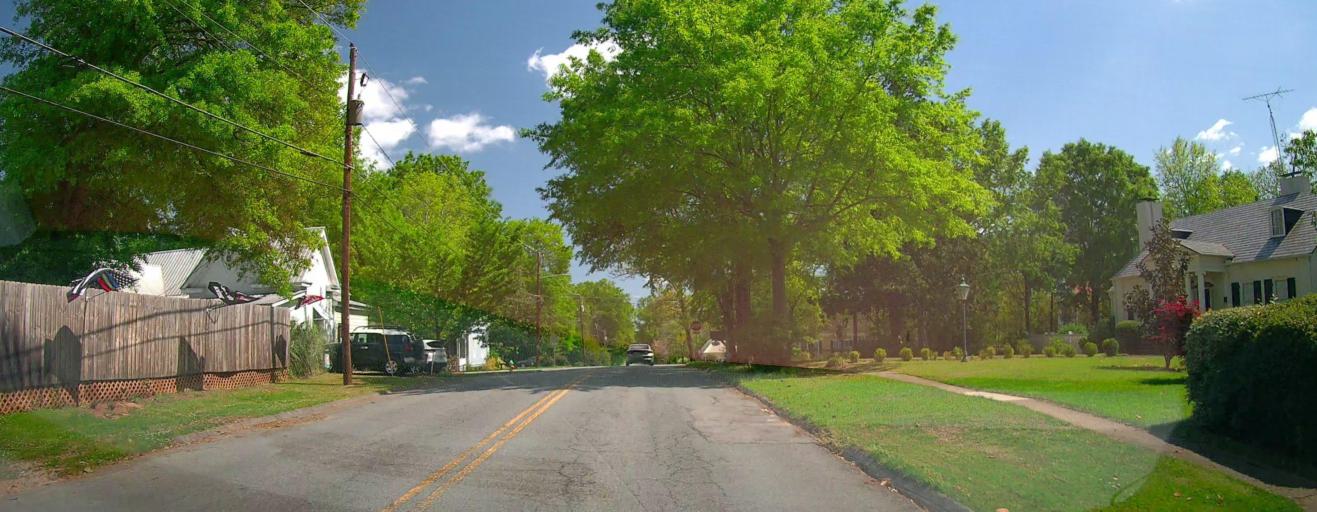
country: US
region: Georgia
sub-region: Putnam County
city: Eatonton
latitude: 33.3251
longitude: -83.3908
